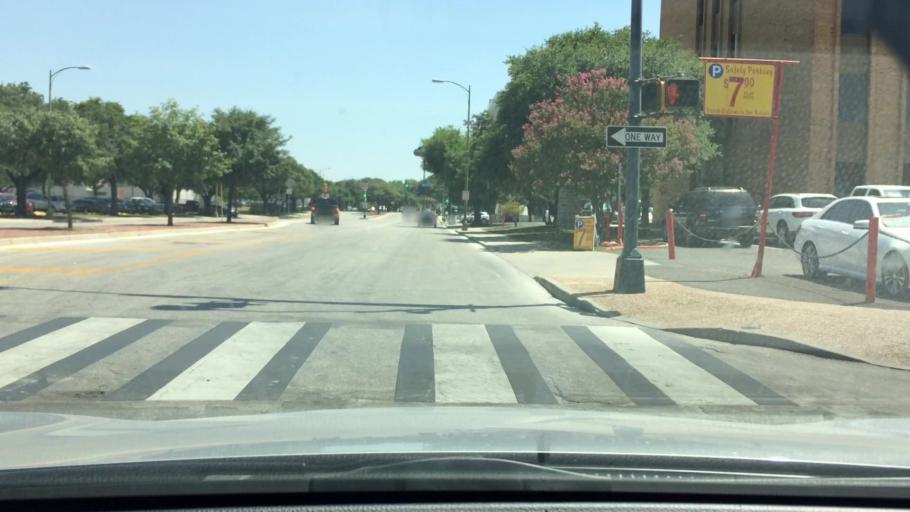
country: US
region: Texas
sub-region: Bexar County
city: San Antonio
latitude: 29.4243
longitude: -98.4984
